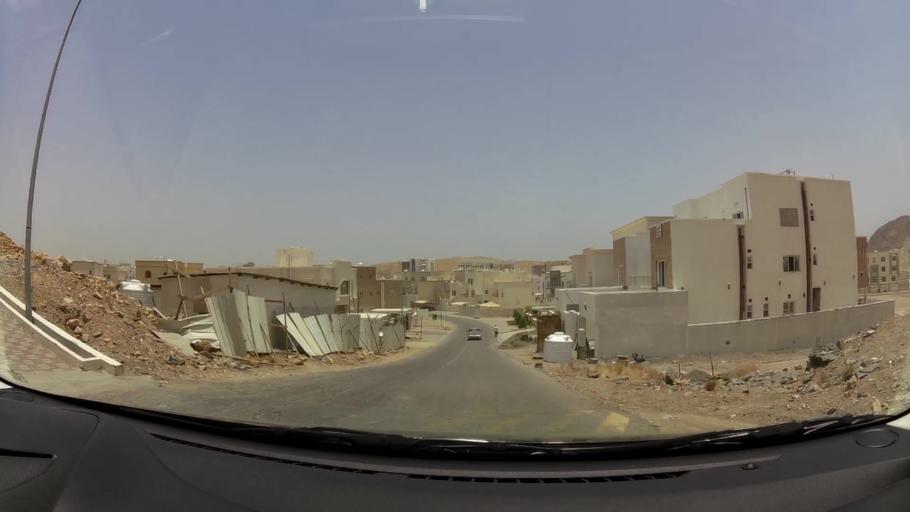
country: OM
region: Muhafazat Masqat
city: Bawshar
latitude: 23.5588
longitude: 58.4177
